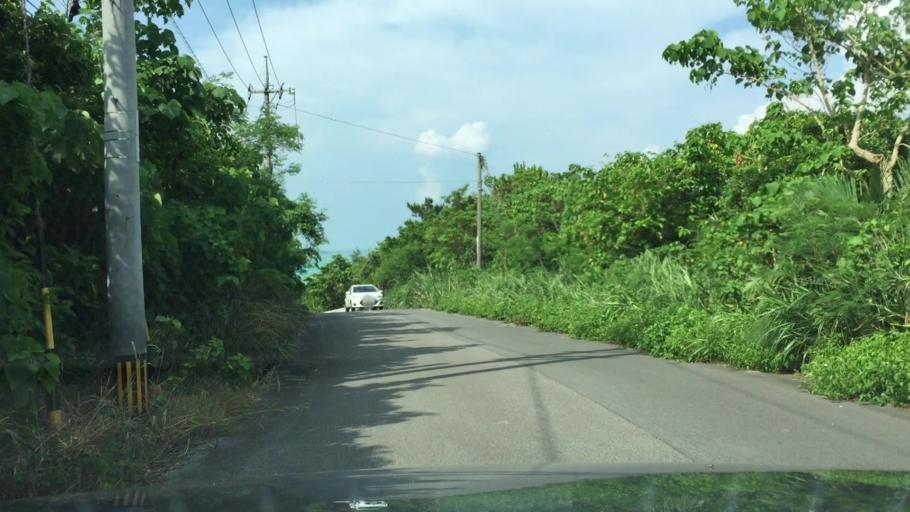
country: JP
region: Okinawa
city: Ishigaki
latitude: 24.4917
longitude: 124.2777
